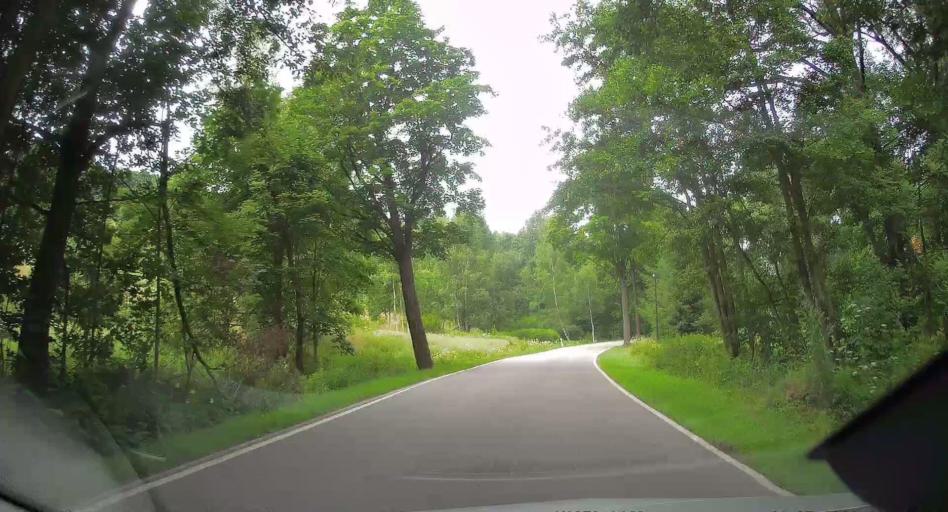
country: PL
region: Lower Silesian Voivodeship
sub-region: Powiat walbrzyski
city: Jedlina-Zdroj
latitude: 50.7286
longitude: 16.3719
